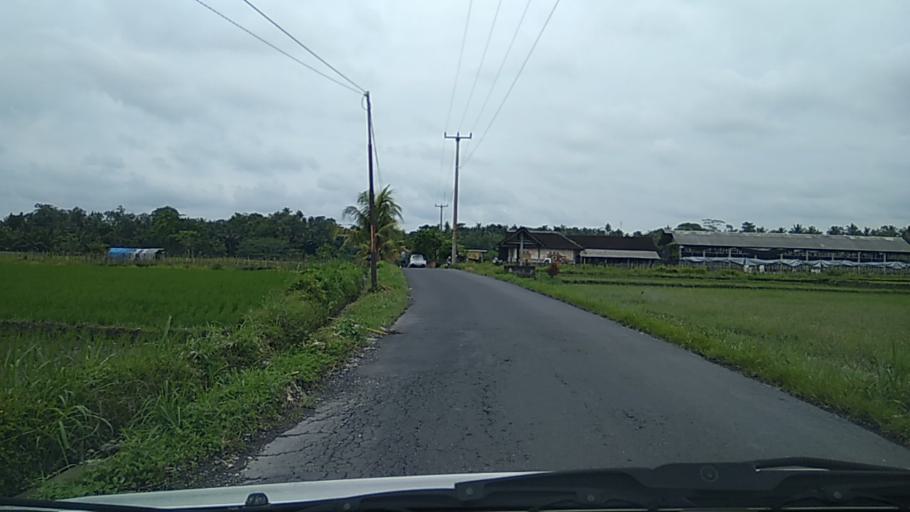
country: ID
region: Bali
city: Banjar Keraman
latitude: -8.5236
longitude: 115.2227
